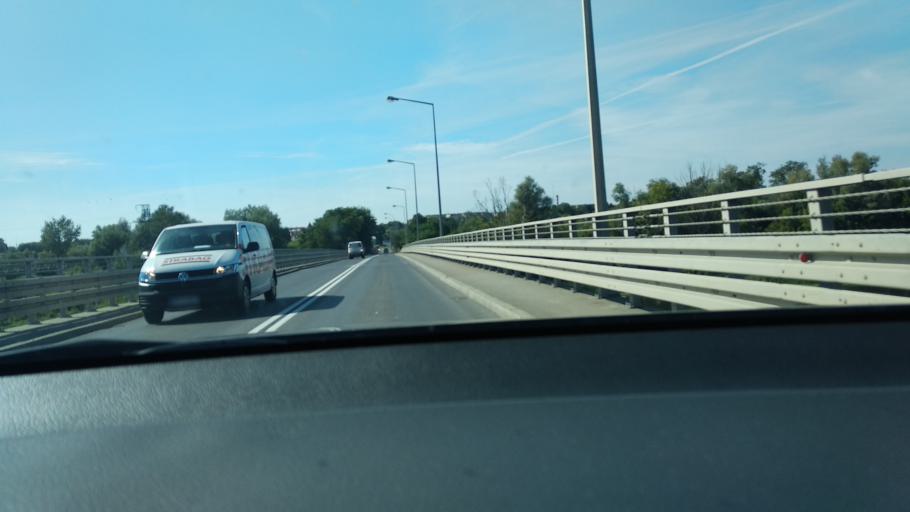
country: PL
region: Masovian Voivodeship
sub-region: Powiat pultuski
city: Pultusk
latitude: 52.6962
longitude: 21.0922
